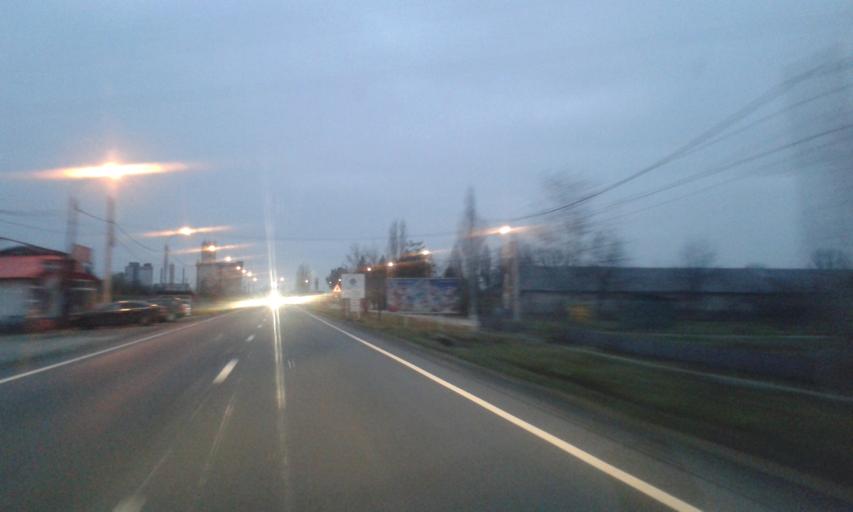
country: RO
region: Gorj
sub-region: Comuna Turcinesti
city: Turcinesti
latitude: 45.0800
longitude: 23.3133
